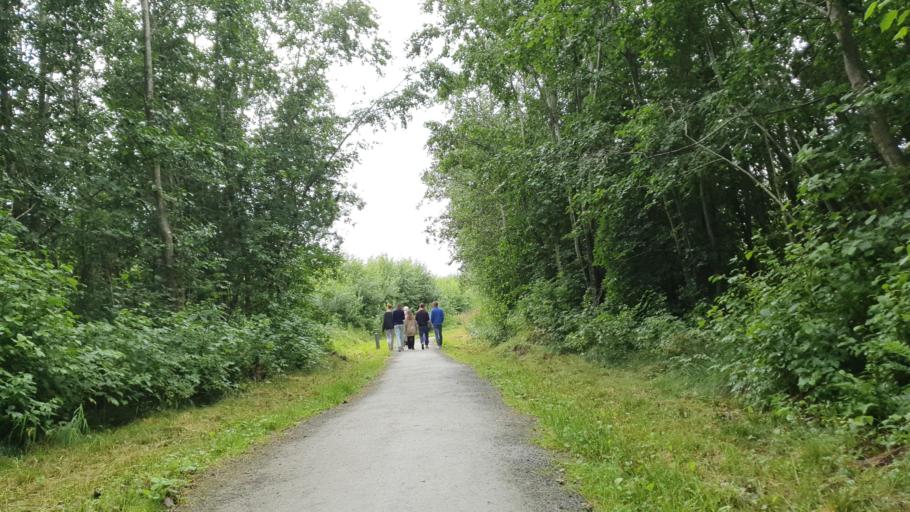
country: NO
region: Sor-Trondelag
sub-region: Selbu
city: Mebonden
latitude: 63.2312
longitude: 11.0239
